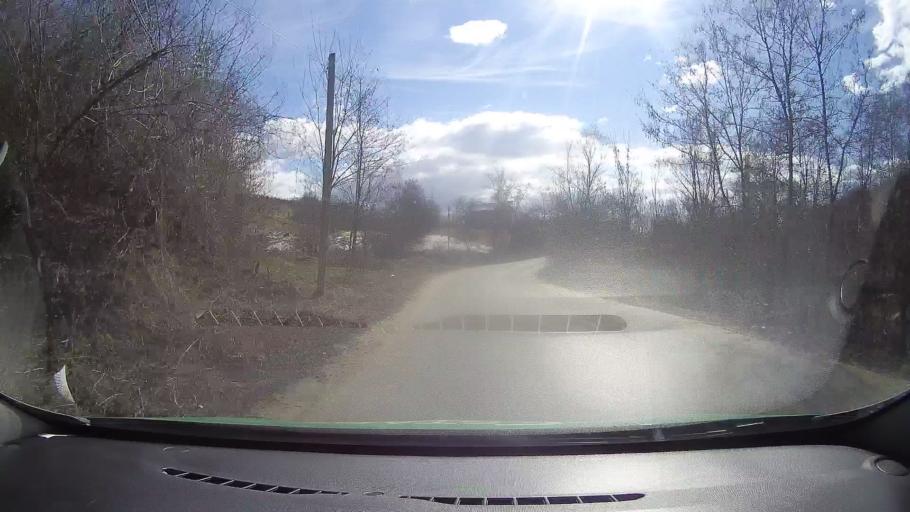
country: RO
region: Dambovita
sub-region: Comuna Vulcana-Pandele
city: Gura Vulcanei
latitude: 45.0393
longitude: 25.3910
